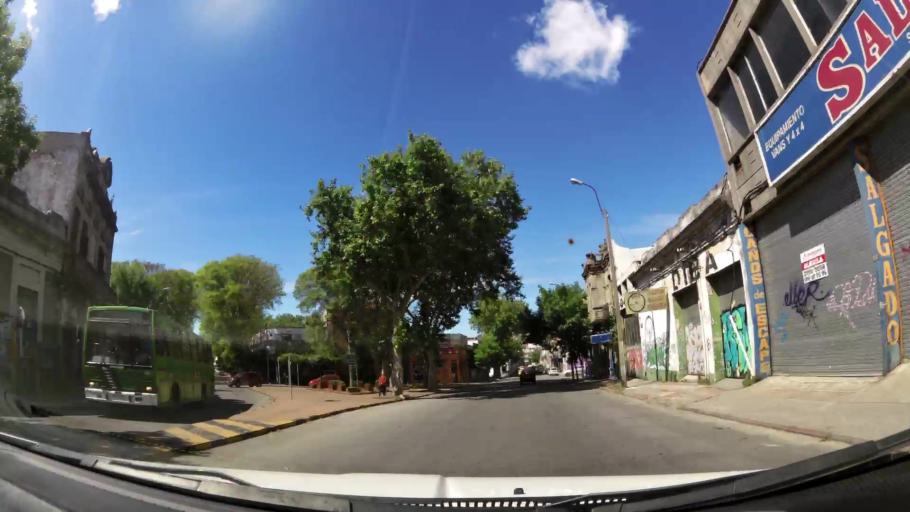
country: UY
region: Montevideo
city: Montevideo
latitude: -34.8959
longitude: -56.1875
